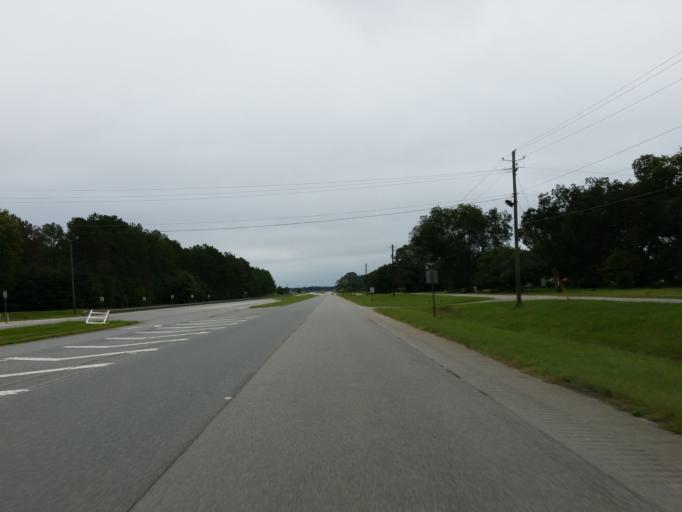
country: US
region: Georgia
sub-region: Houston County
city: Perry
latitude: 32.4302
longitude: -83.7436
